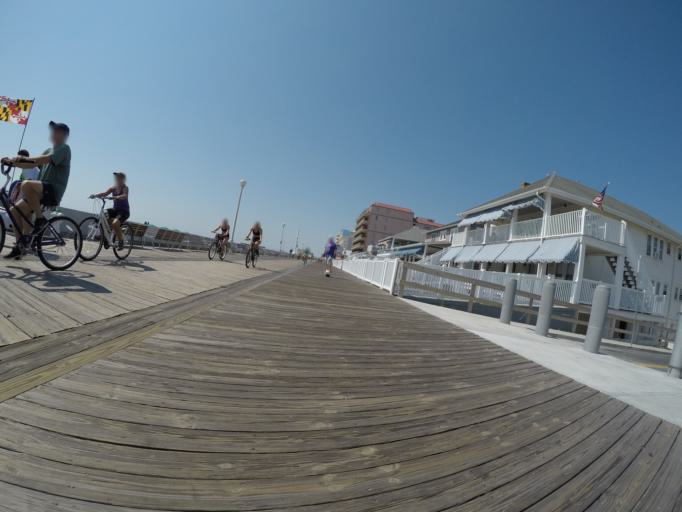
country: US
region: Maryland
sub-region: Worcester County
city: Ocean City
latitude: 38.3410
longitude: -75.0798
